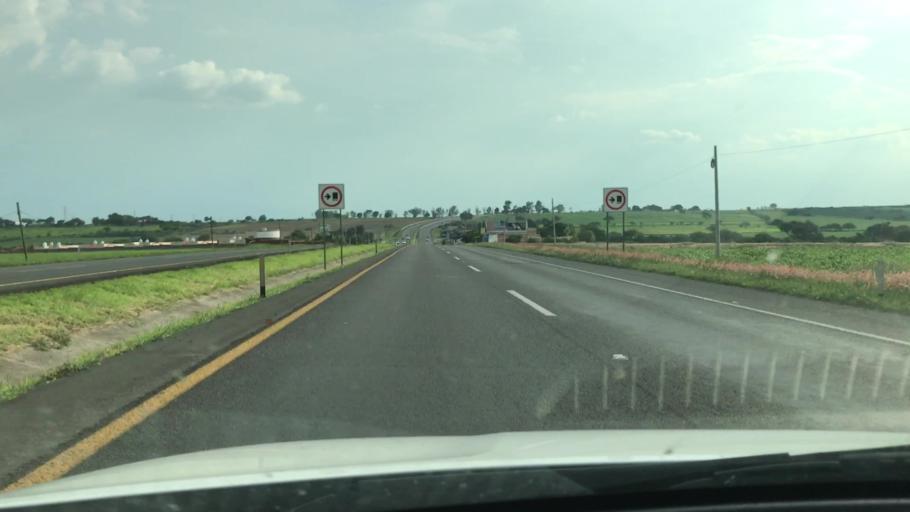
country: MX
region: Guanajuato
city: Penjamo
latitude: 20.3922
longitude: -101.7611
